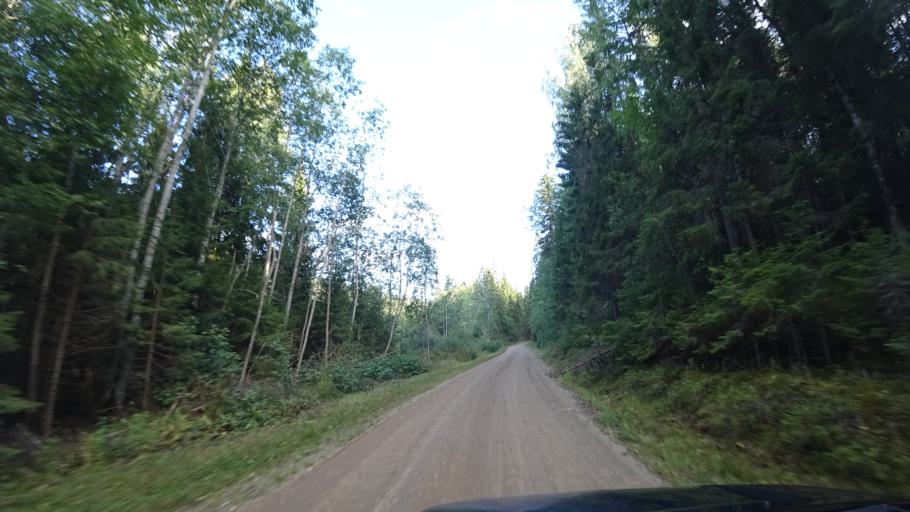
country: FI
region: Paijanne Tavastia
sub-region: Lahti
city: Auttoinen
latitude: 61.2187
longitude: 25.2106
